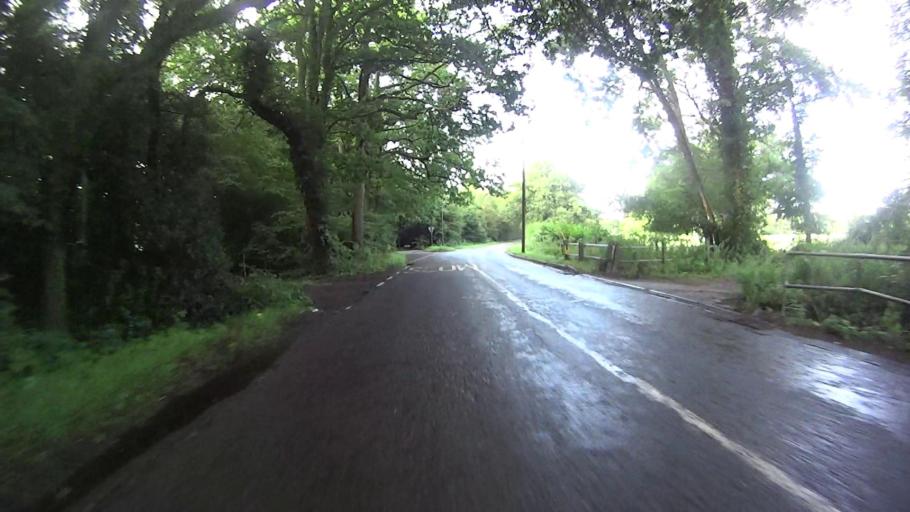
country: GB
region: England
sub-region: Surrey
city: Lingfield
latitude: 51.1680
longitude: -0.0171
